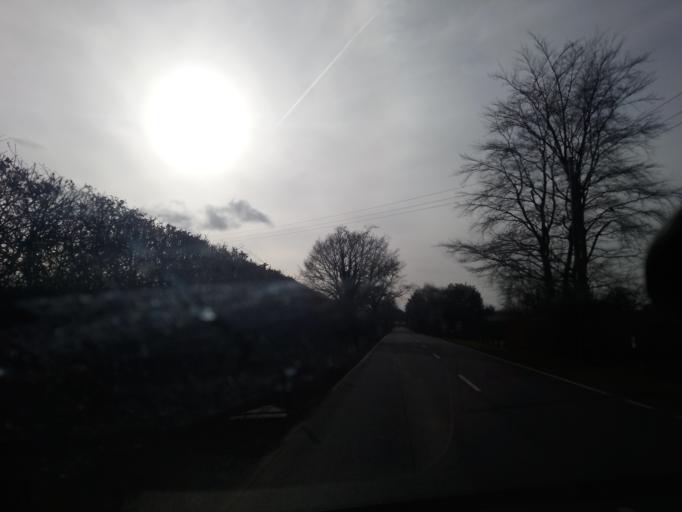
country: GB
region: England
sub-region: Shropshire
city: Prees
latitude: 52.8840
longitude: -2.6441
